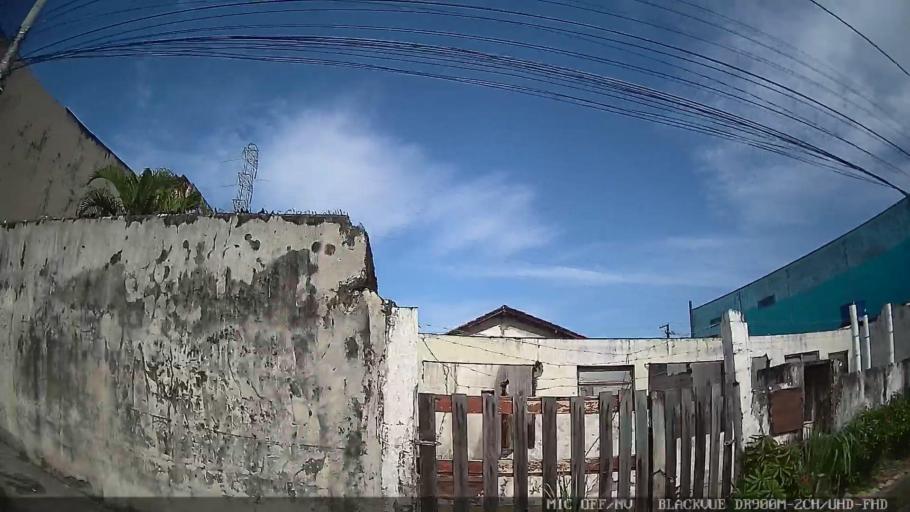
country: BR
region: Sao Paulo
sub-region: Itanhaem
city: Itanhaem
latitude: -24.1636
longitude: -46.7594
